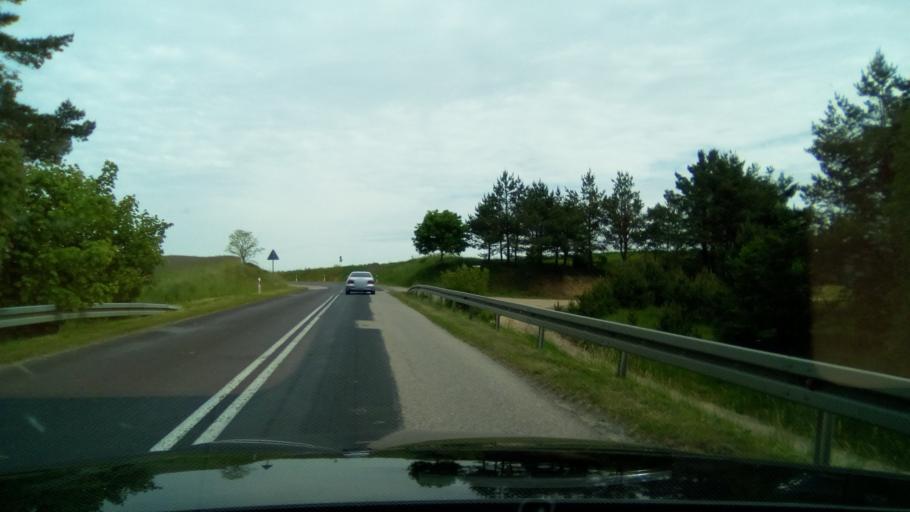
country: PL
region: Pomeranian Voivodeship
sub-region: Powiat bytowski
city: Lipnica
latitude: 54.0606
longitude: 17.4268
